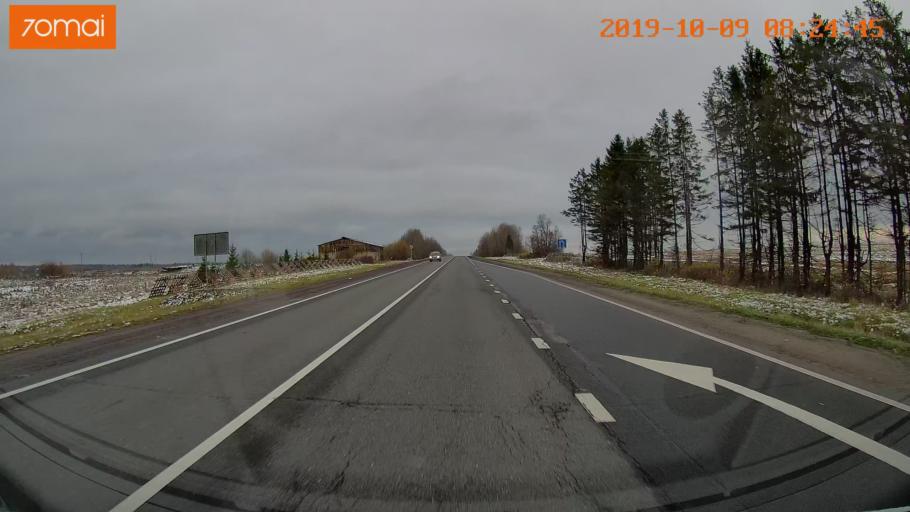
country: RU
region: Vologda
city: Gryazovets
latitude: 58.7709
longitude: 40.2765
